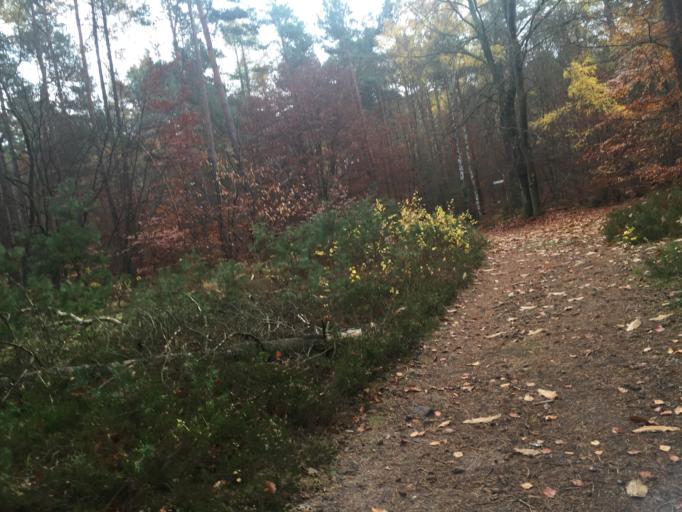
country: DE
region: Rheinland-Pfalz
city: Carlsberg
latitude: 49.4864
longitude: 8.0229
